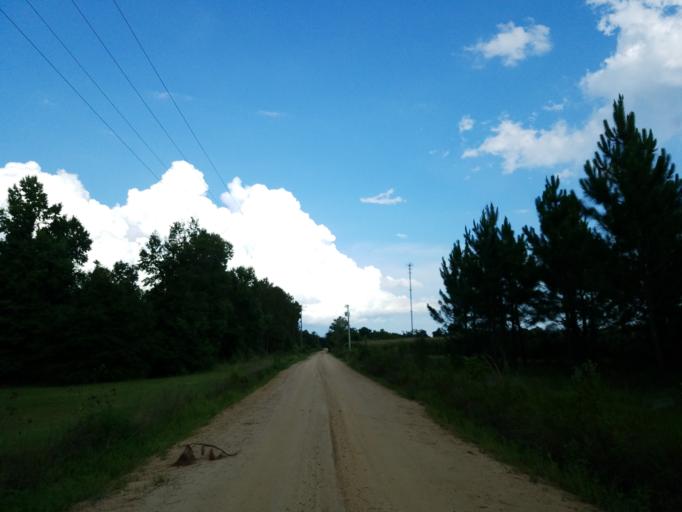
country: US
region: Georgia
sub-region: Turner County
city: Ashburn
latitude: 31.7454
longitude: -83.6635
